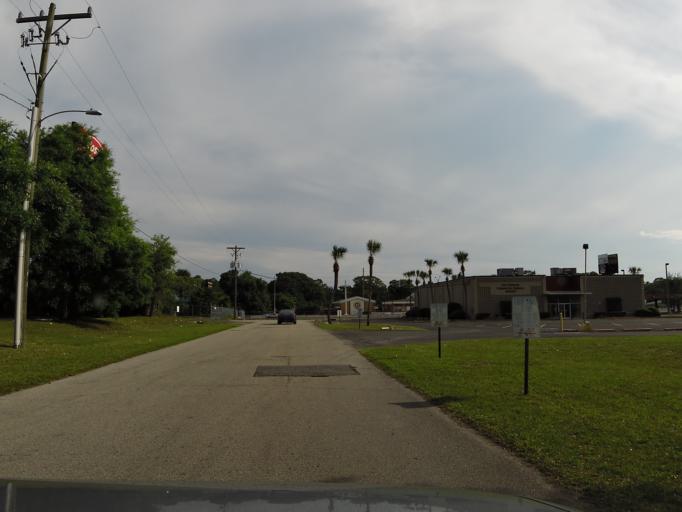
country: US
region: Florida
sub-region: Duval County
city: Jacksonville
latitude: 30.3288
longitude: -81.5891
